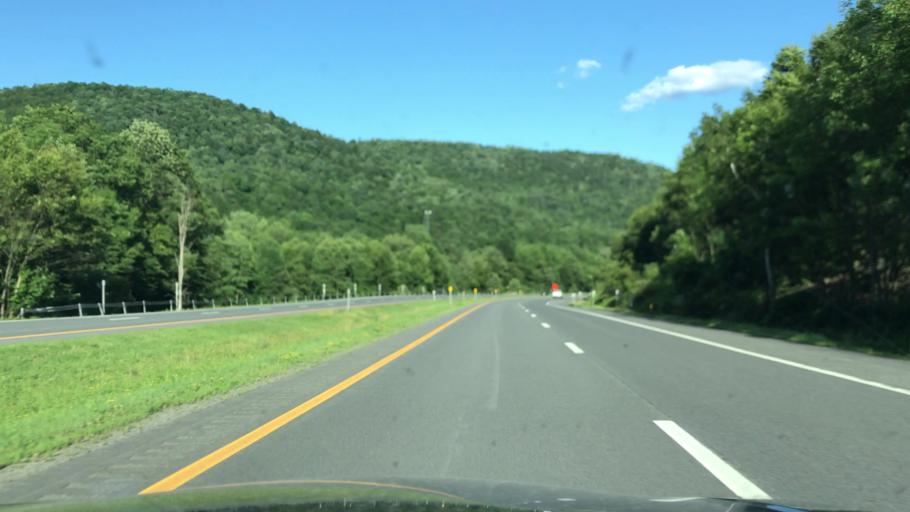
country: US
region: New York
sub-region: Delaware County
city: Walton
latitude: 41.9828
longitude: -75.0606
